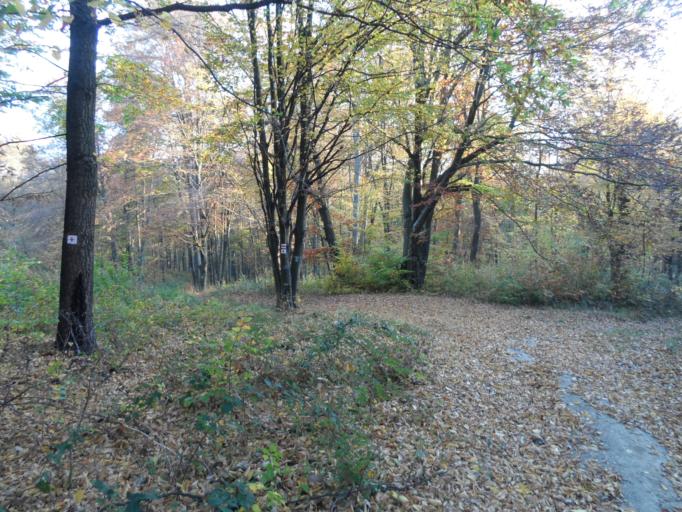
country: HU
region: Veszprem
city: Herend
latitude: 47.2027
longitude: 17.7005
